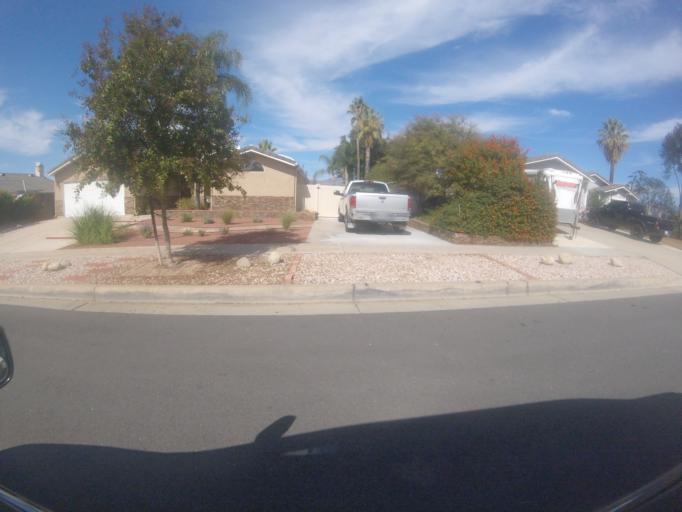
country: US
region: California
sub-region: San Bernardino County
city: Mentone
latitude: 34.0537
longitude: -117.1525
